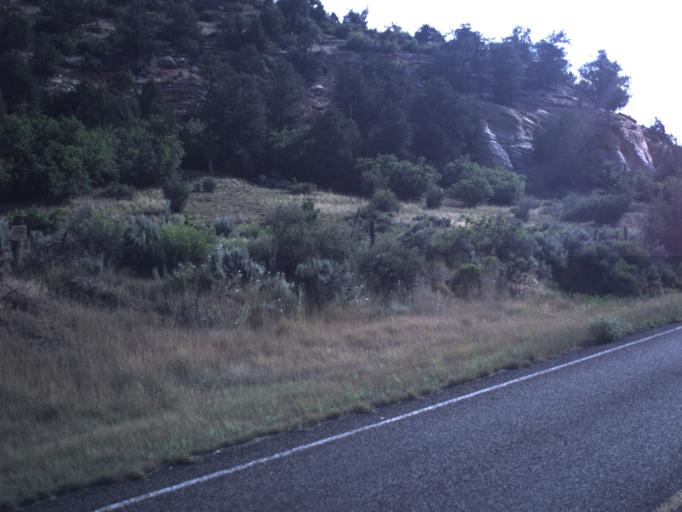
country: US
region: Utah
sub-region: Washington County
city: Hildale
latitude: 37.2381
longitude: -112.8412
